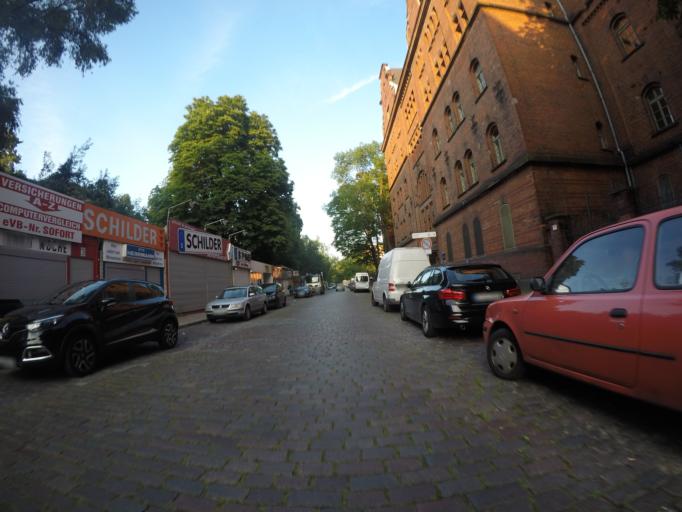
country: DE
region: Berlin
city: Bezirk Kreuzberg
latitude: 52.4864
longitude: 13.3975
